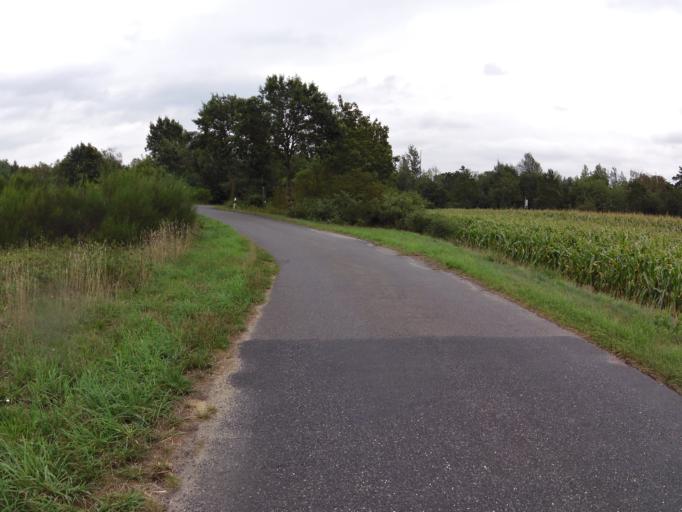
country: DE
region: Lower Saxony
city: Rotenburg
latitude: 53.1343
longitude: 9.4430
